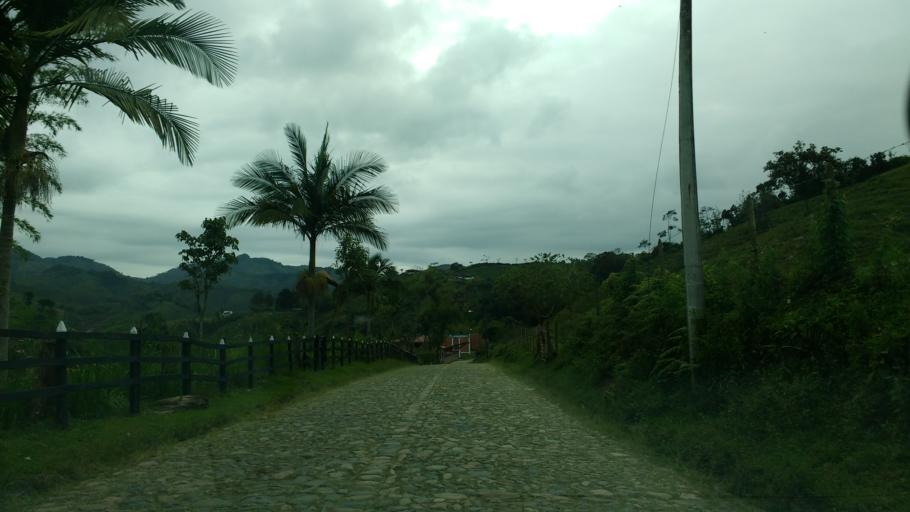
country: CO
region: Antioquia
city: Concepcion
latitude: 6.3922
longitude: -75.2578
